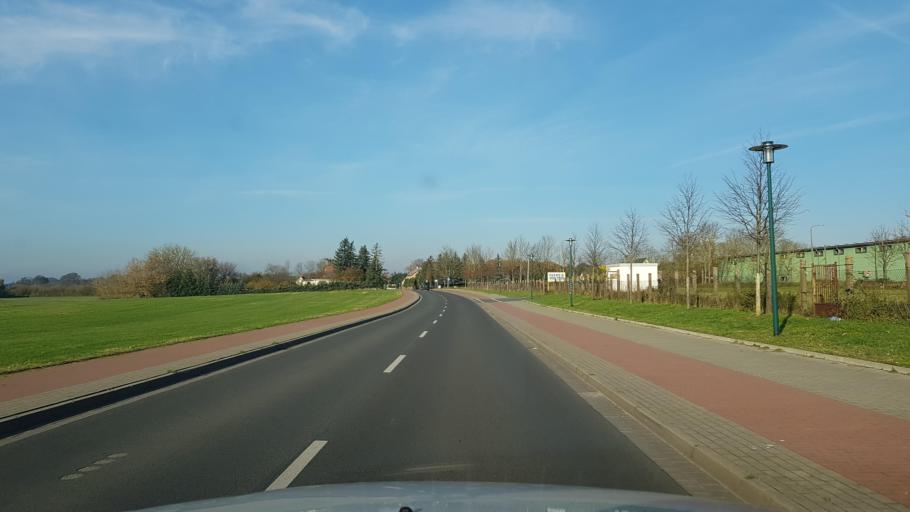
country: DE
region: Brandenburg
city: Brussow
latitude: 53.4606
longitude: 14.2073
